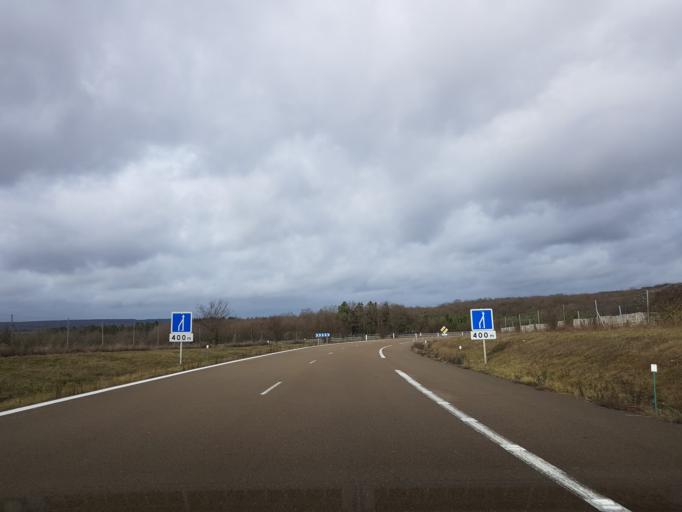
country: FR
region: Champagne-Ardenne
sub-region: Departement de la Haute-Marne
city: Rolampont
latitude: 47.9150
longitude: 5.2264
